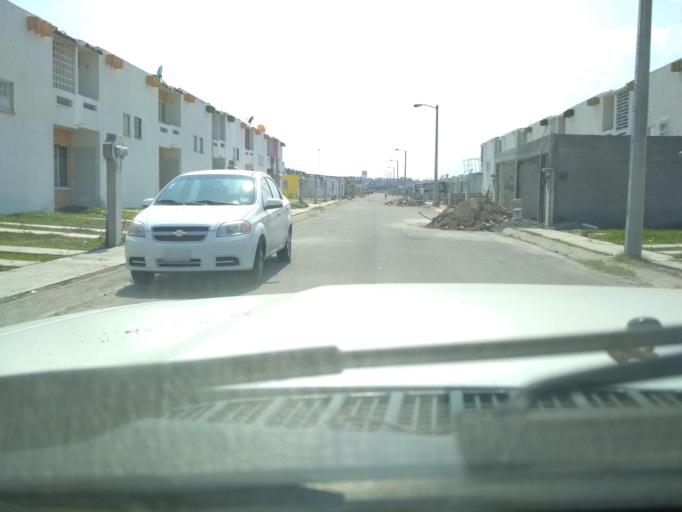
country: MX
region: Veracruz
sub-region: Veracruz
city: Lomas de Rio Medio Cuatro
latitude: 19.1903
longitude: -96.2092
